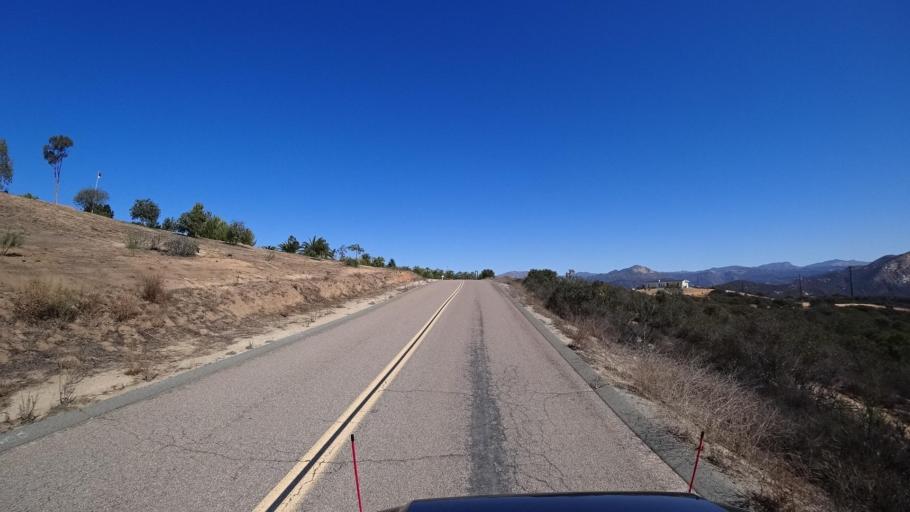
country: US
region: California
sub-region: San Diego County
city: Harbison Canyon
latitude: 32.7980
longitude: -116.7919
